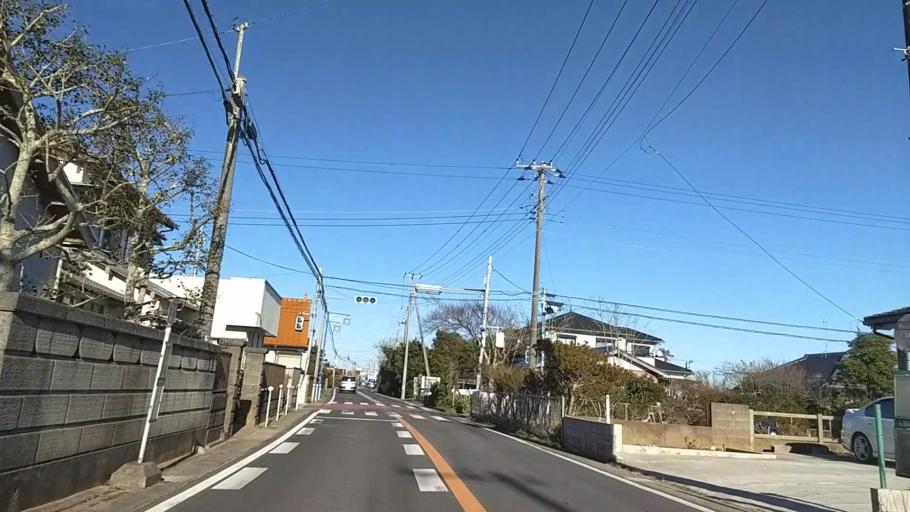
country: JP
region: Chiba
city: Naruto
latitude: 35.5470
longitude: 140.4590
